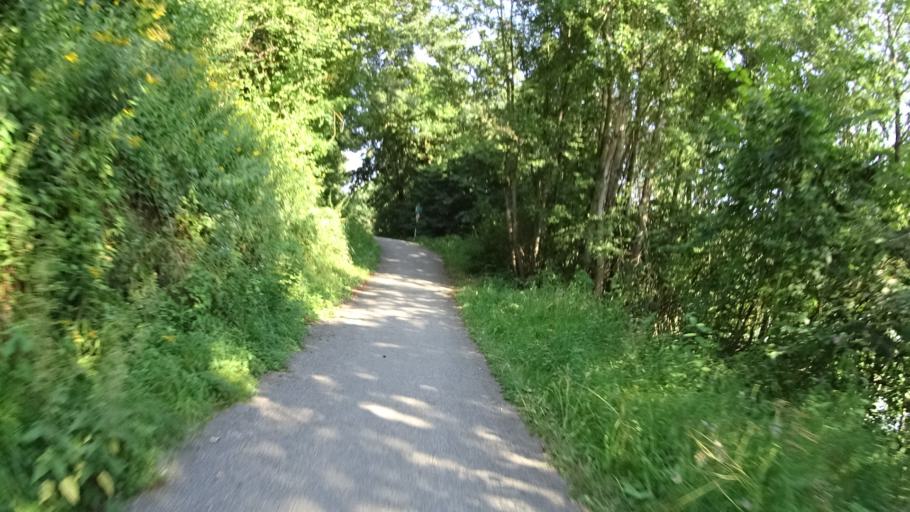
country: AT
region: Carinthia
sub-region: Politischer Bezirk Villach Land
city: Wernberg
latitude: 46.5975
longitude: 13.9517
